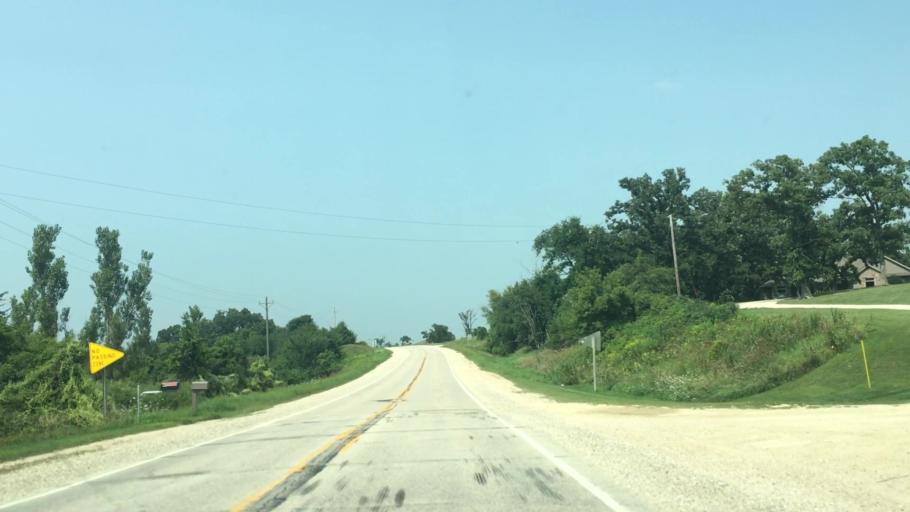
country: US
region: Iowa
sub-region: Fayette County
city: West Union
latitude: 43.1142
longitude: -91.8692
